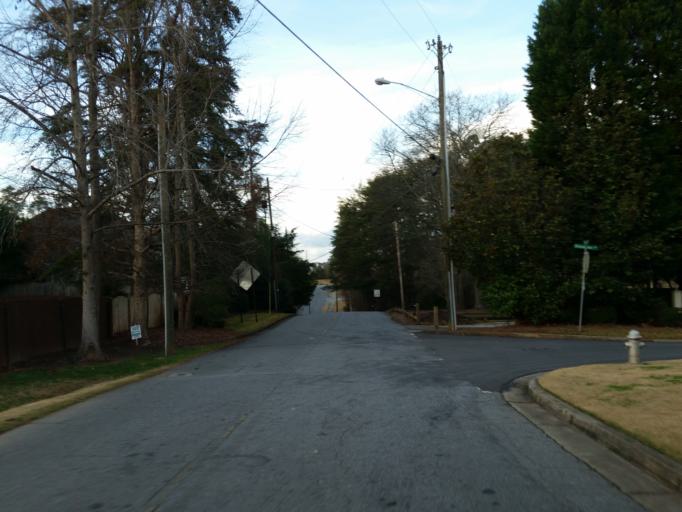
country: US
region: Georgia
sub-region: Cobb County
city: Marietta
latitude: 33.9799
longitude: -84.4865
